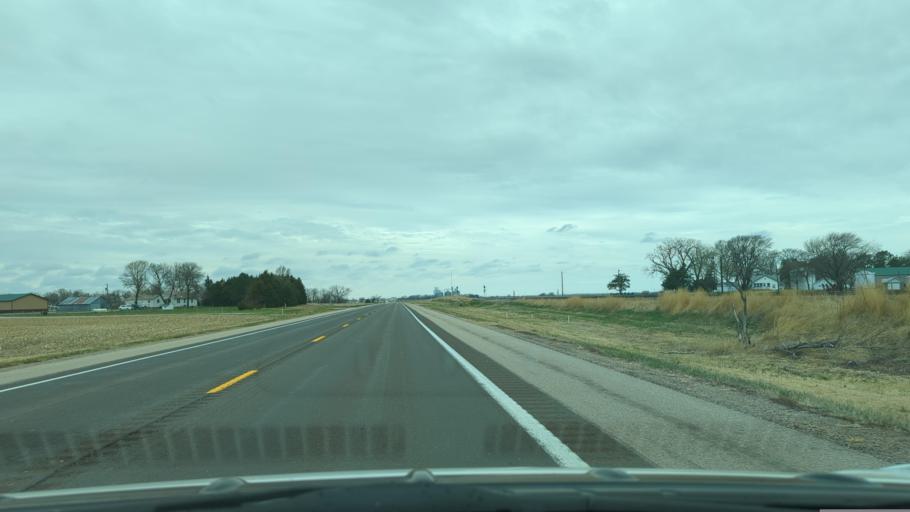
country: US
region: Nebraska
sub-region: Lancaster County
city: Waverly
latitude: 40.9378
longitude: -96.4859
